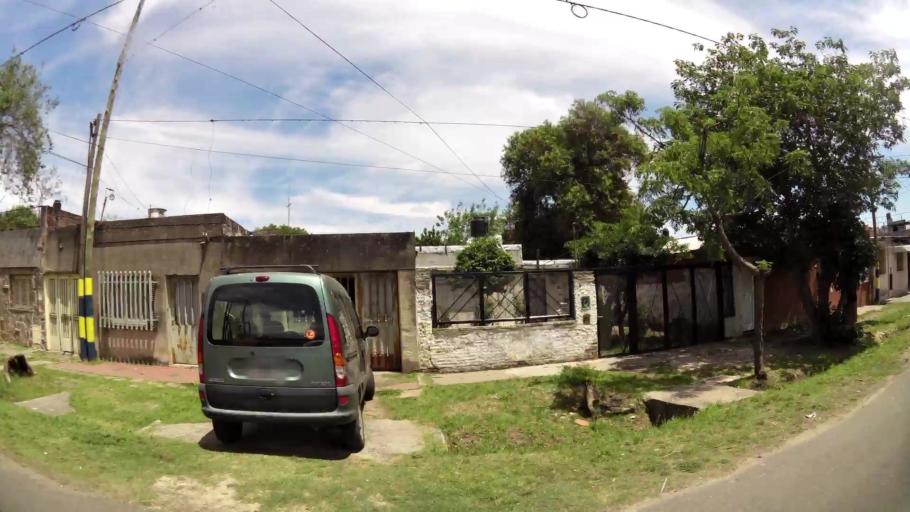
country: AR
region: Santa Fe
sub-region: Departamento de Rosario
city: Rosario
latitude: -32.9875
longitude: -60.6252
